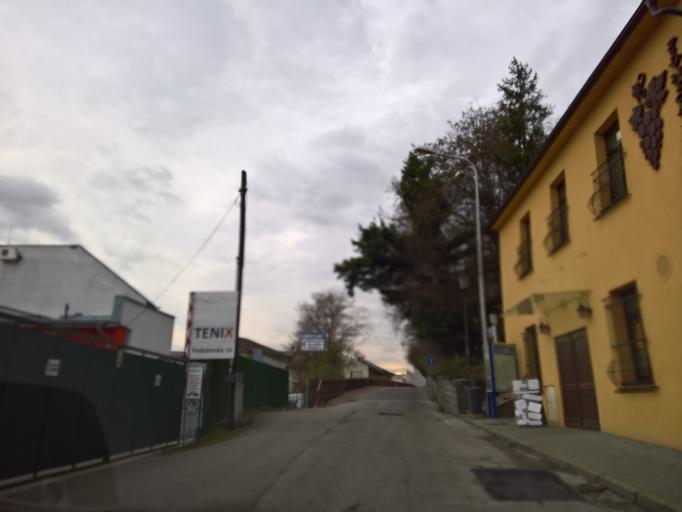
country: SK
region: Nitriansky
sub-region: Okres Nitra
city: Nitra
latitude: 48.3161
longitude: 18.0899
